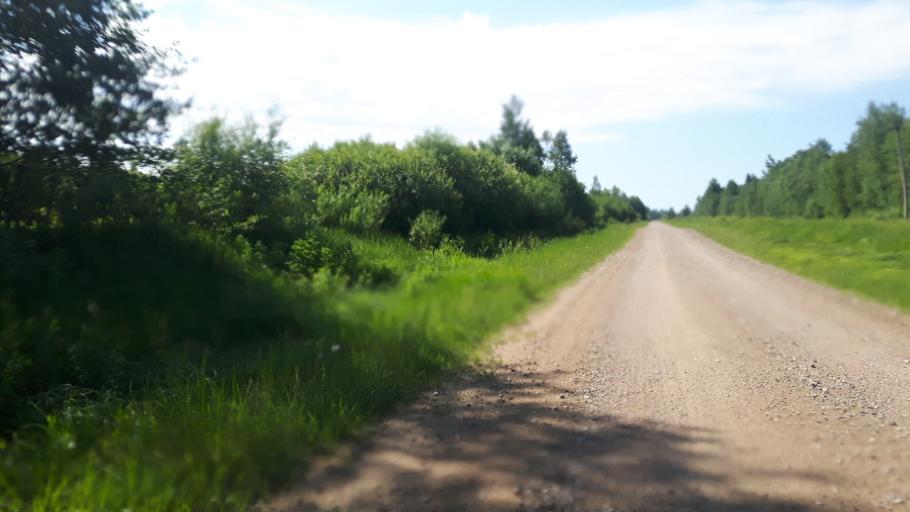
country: EE
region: Paernumaa
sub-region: Vaendra vald (alev)
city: Vandra
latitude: 58.6818
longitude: 25.0334
